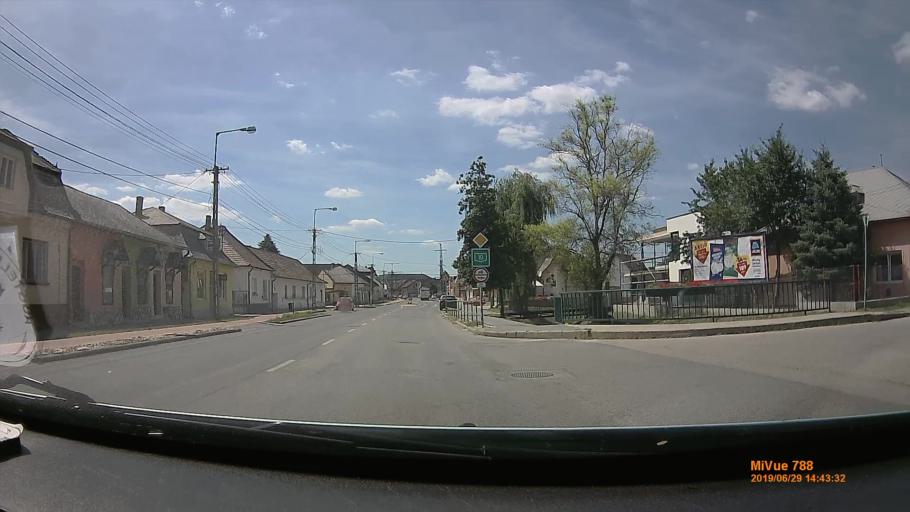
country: HU
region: Komarom-Esztergom
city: Nyergesujfalu
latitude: 47.7605
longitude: 18.5561
